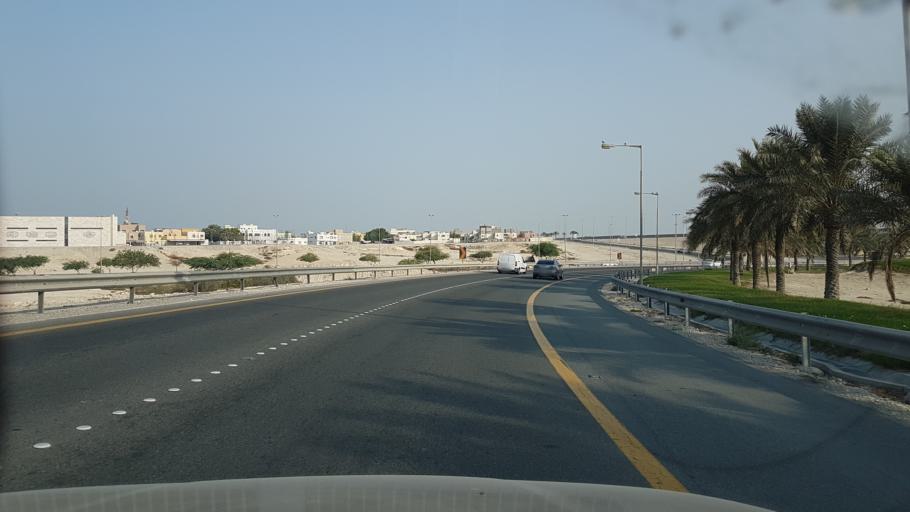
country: BH
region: Central Governorate
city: Dar Kulayb
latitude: 26.0574
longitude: 50.5160
